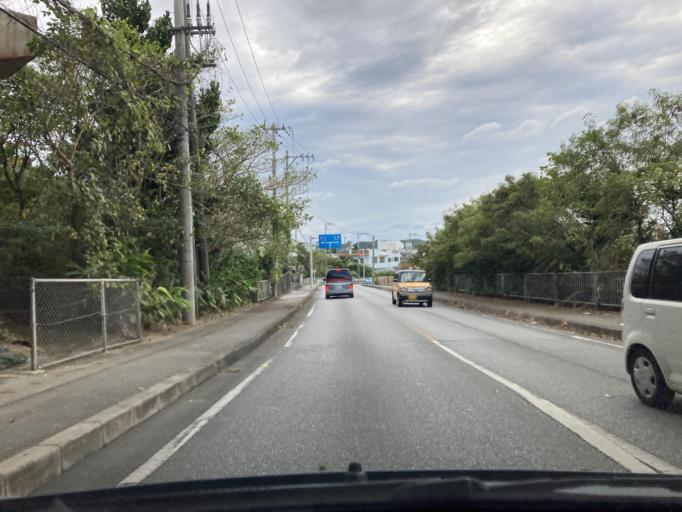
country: JP
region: Okinawa
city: Ishikawa
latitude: 26.4384
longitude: 127.8037
